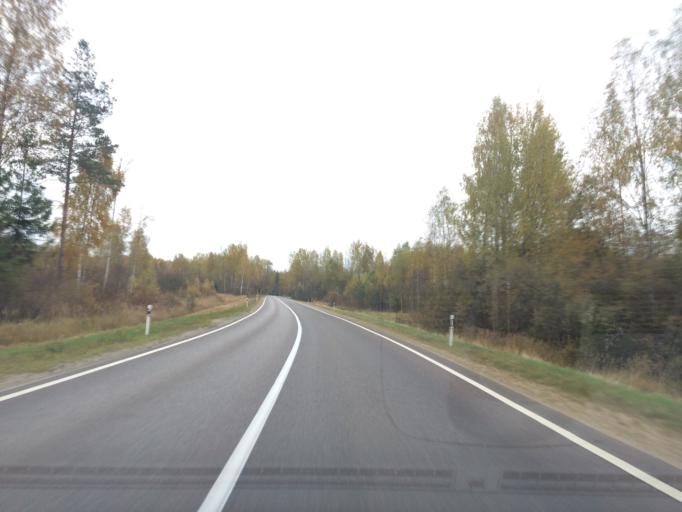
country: LV
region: Livani
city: Livani
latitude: 56.5299
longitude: 26.1446
